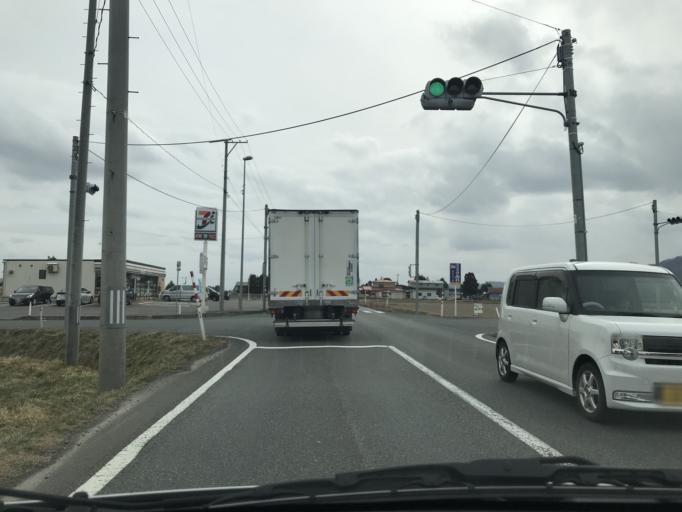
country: JP
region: Iwate
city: Morioka-shi
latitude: 39.5578
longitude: 141.1345
